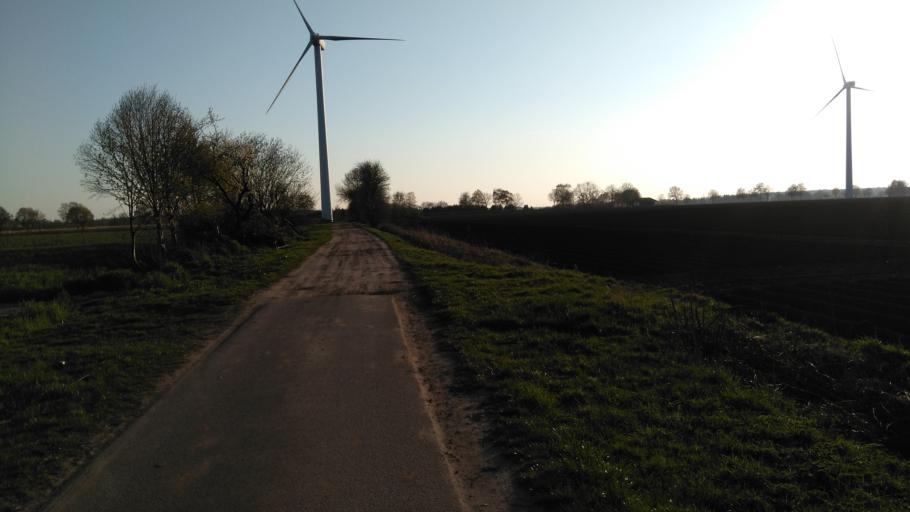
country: DE
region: Lower Saxony
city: Apensen
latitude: 53.4523
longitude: 9.5913
